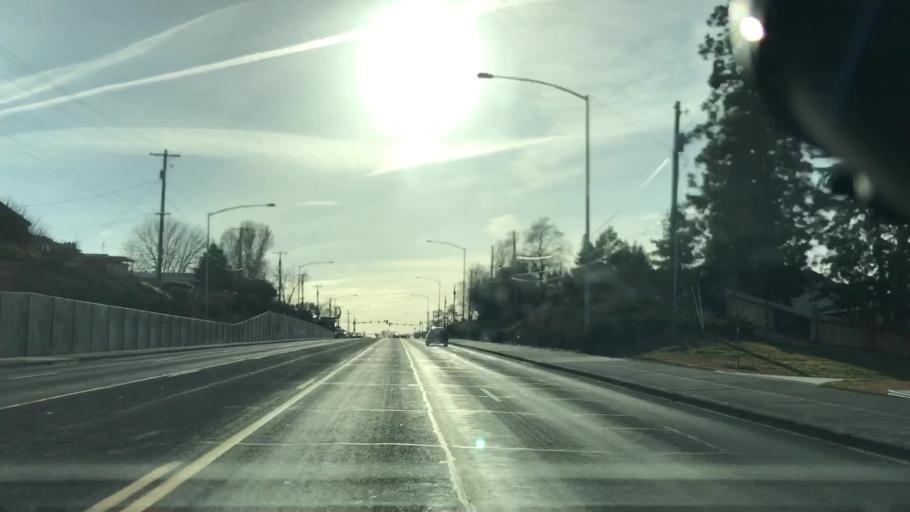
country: US
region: Washington
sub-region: Grant County
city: Moses Lake
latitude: 47.1241
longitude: -119.2684
